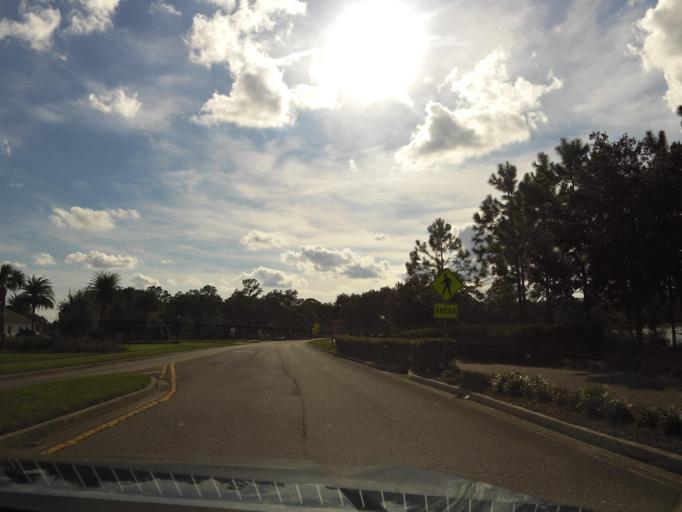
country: US
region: Florida
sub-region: Clay County
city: Green Cove Springs
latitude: 29.9304
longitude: -81.5044
